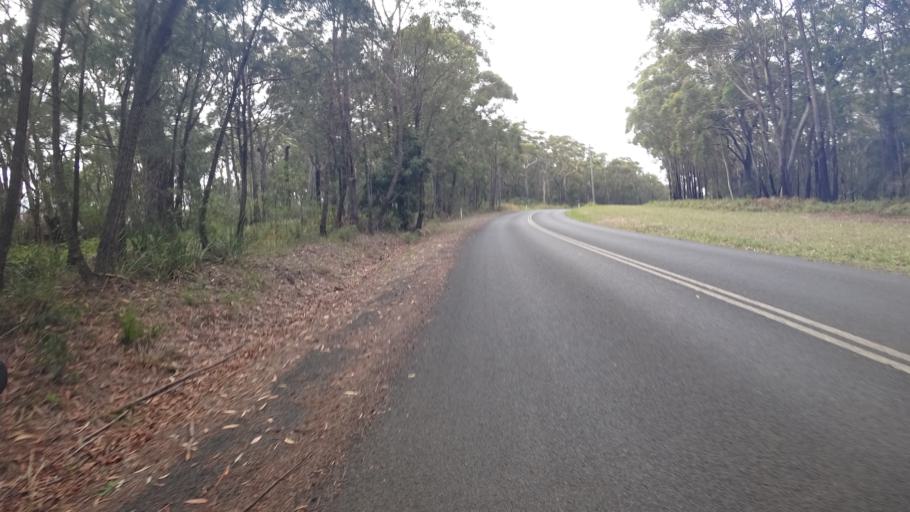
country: AU
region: New South Wales
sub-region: Shoalhaven Shire
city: Milton
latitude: -35.2603
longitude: 150.5056
